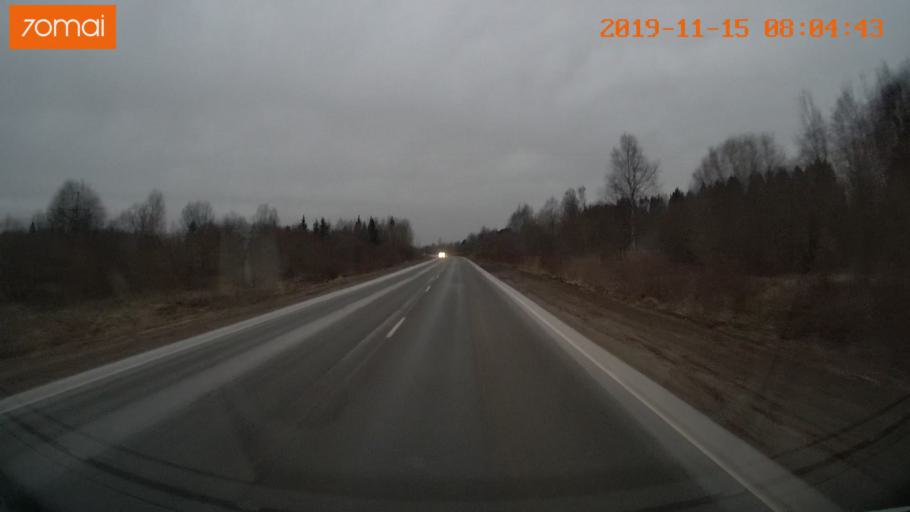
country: RU
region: Vologda
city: Cherepovets
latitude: 59.0110
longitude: 38.0712
